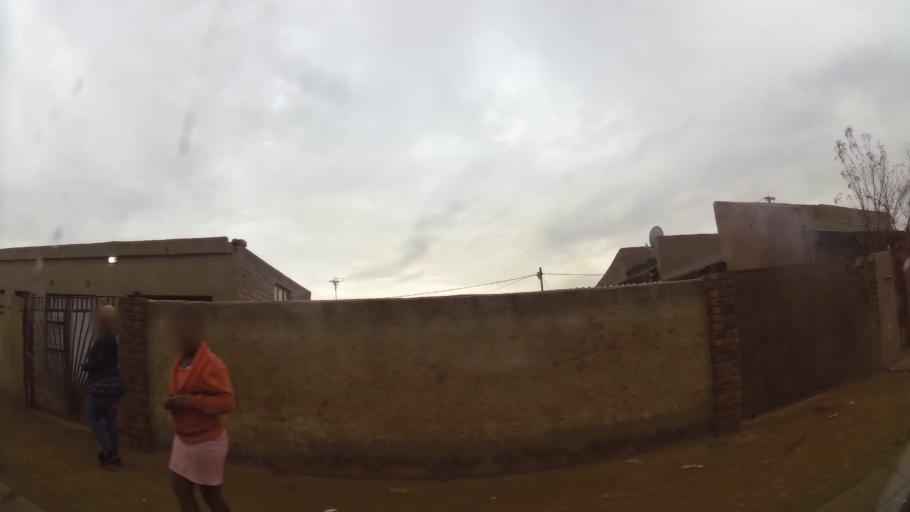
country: ZA
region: Gauteng
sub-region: Ekurhuleni Metropolitan Municipality
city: Germiston
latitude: -26.3819
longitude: 28.1773
